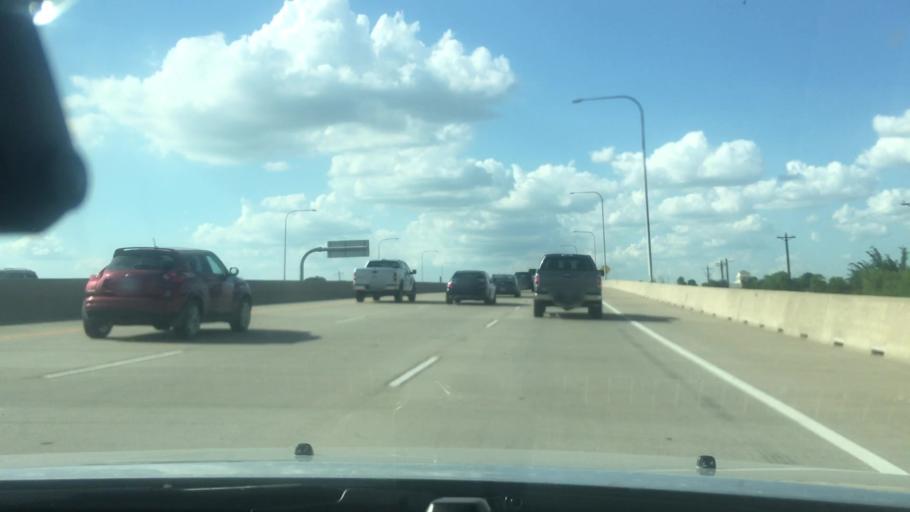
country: US
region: Texas
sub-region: Collin County
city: Frisco
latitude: 33.1434
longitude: -96.8389
